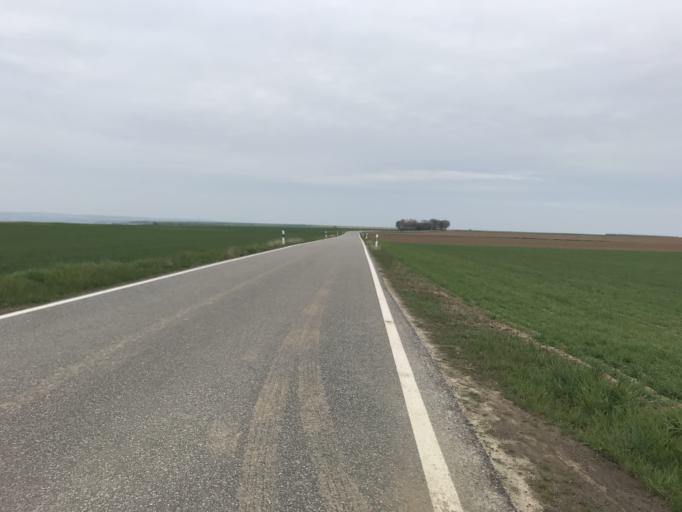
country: DE
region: Rheinland-Pfalz
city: Nieder-Hilbersheim
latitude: 49.9115
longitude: 8.0537
